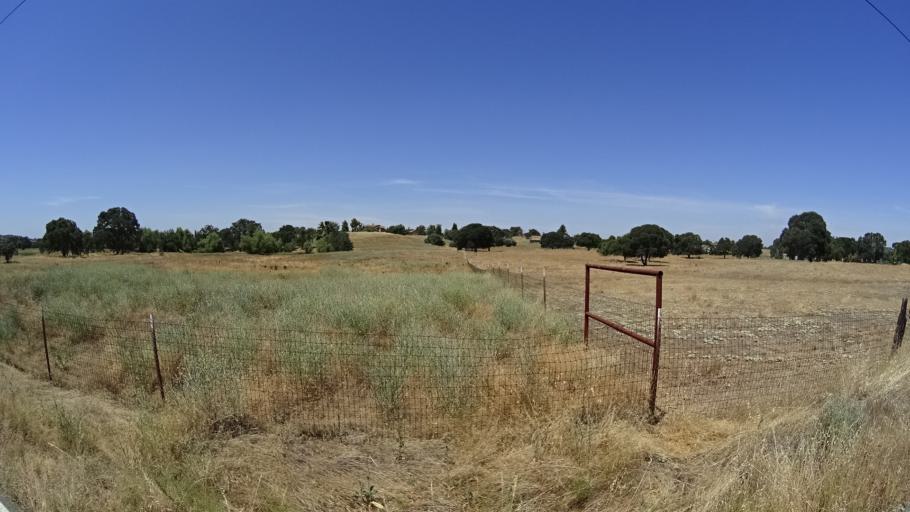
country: US
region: California
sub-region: Calaveras County
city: Rancho Calaveras
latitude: 38.1728
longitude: -120.9180
